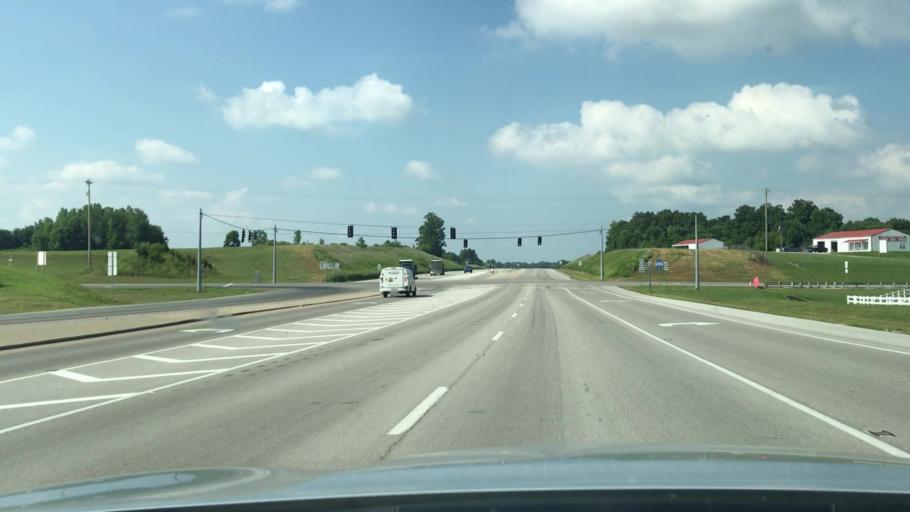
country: US
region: Kentucky
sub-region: Barren County
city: Glasgow
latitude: 37.0130
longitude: -85.9525
